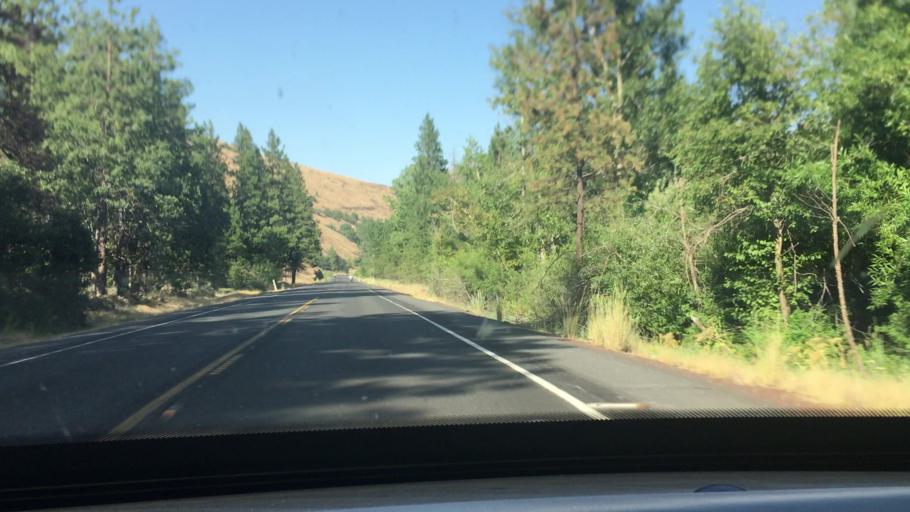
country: US
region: Washington
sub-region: Klickitat County
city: Goldendale
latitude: 46.0342
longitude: -120.5924
